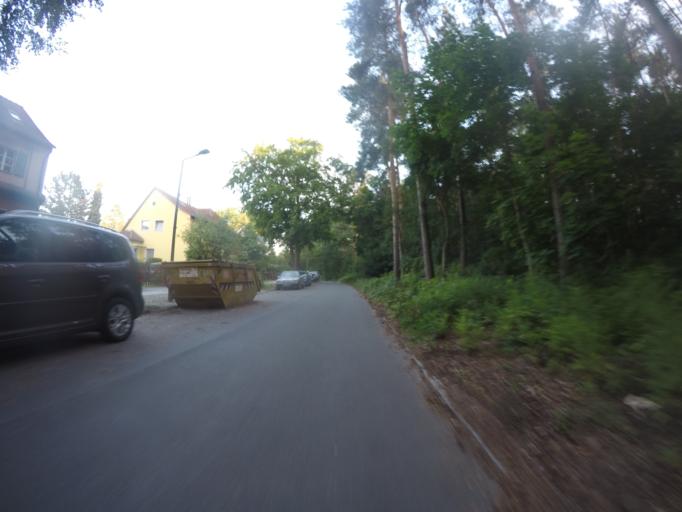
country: DE
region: Berlin
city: Grunewald
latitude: 52.4918
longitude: 13.2577
